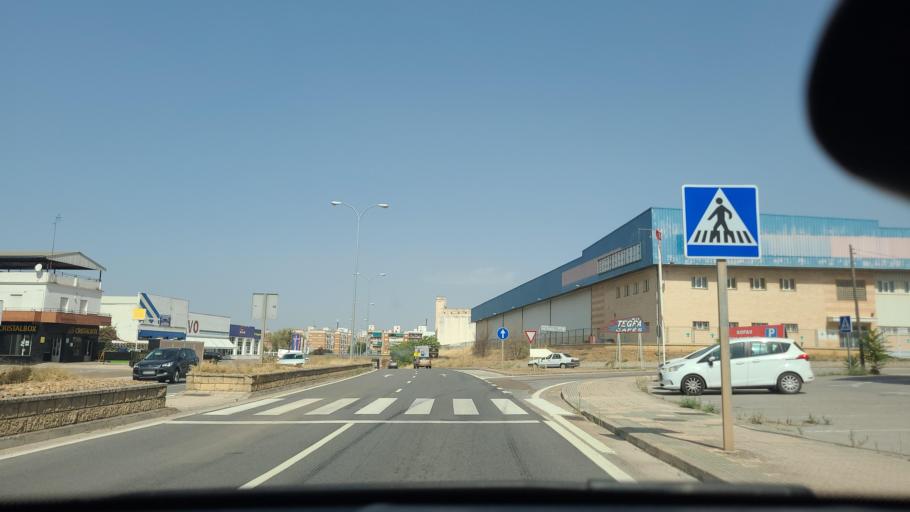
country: ES
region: Extremadura
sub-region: Provincia de Badajoz
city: Zafra
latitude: 38.4210
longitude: -6.4080
